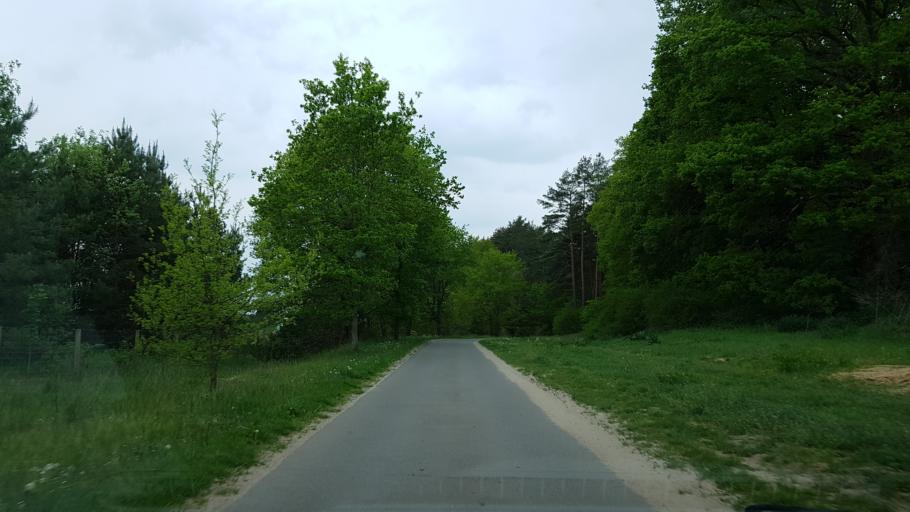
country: DE
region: Lower Saxony
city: Gartow
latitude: 53.0546
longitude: 11.4503
